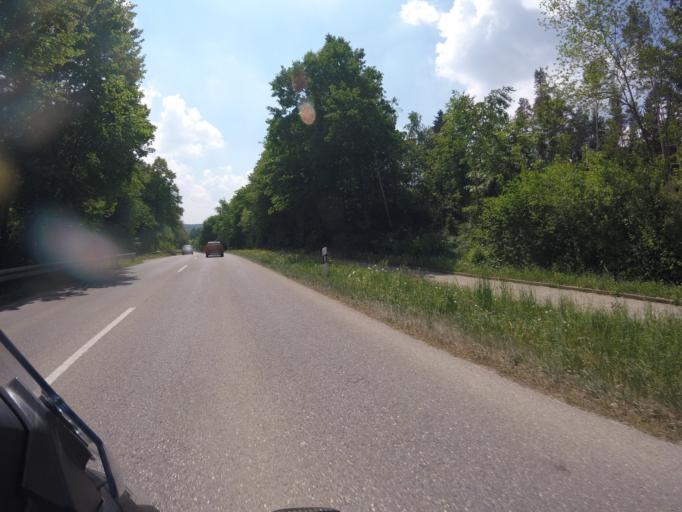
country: DE
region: Bavaria
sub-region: Upper Bavaria
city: Pfaffenhofen an der Ilm
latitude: 48.5312
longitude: 11.4823
